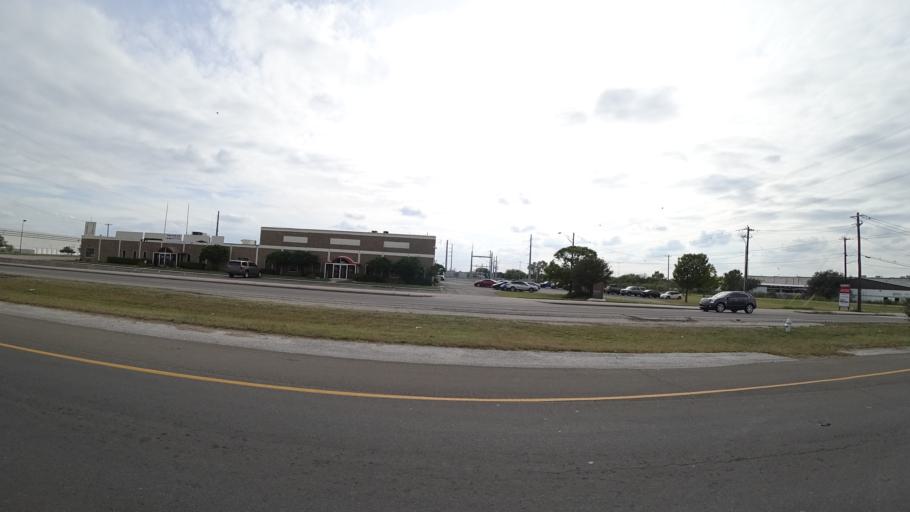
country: US
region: Texas
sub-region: Travis County
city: Wells Branch
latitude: 30.4214
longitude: -97.6648
